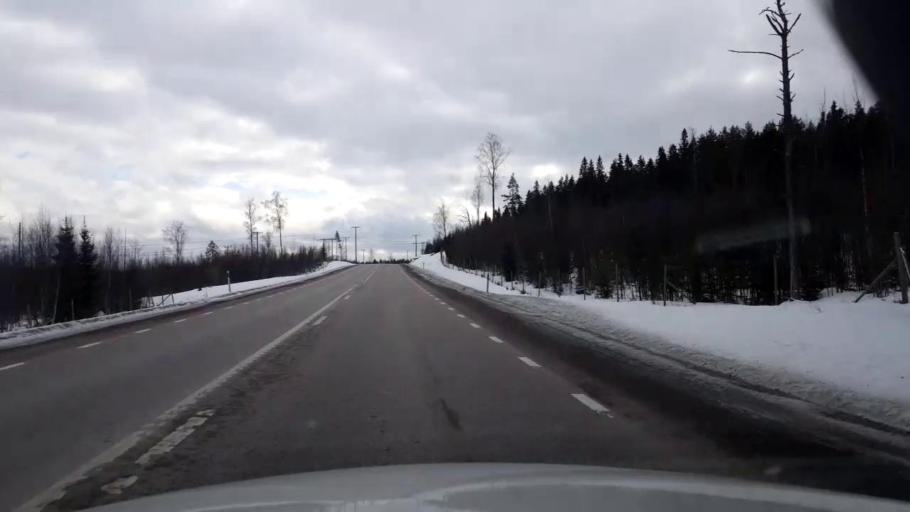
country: SE
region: Gaevleborg
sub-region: Nordanstigs Kommun
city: Bergsjoe
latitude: 62.0037
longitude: 17.2374
